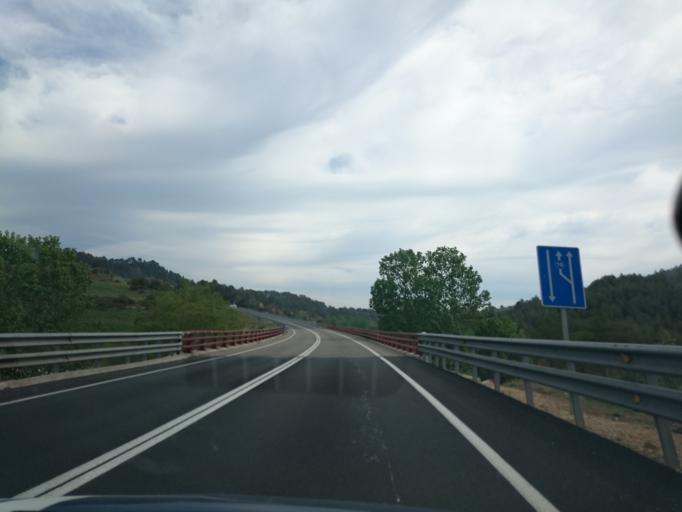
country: ES
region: Catalonia
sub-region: Provincia de Barcelona
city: Sant Salvador de Guardiola
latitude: 41.6722
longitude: 1.7524
